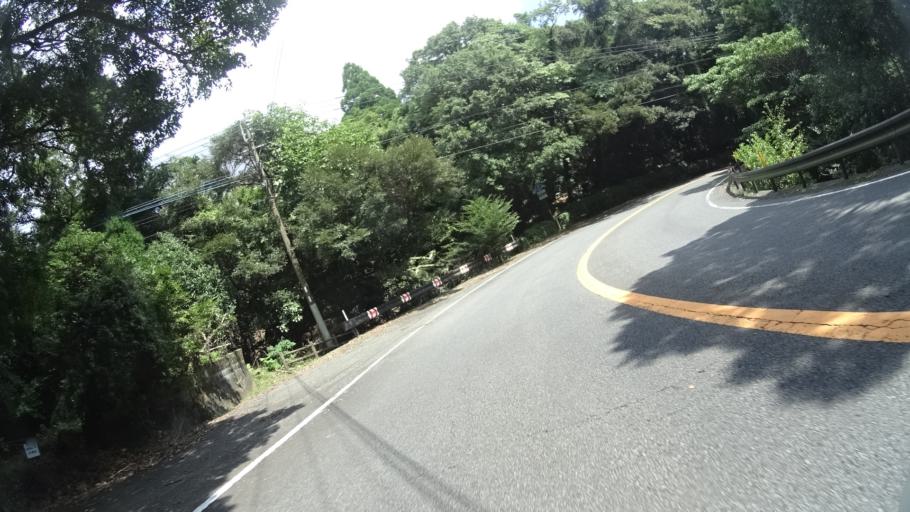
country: JP
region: Miyazaki
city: Kobayashi
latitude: 31.9002
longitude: 130.8343
